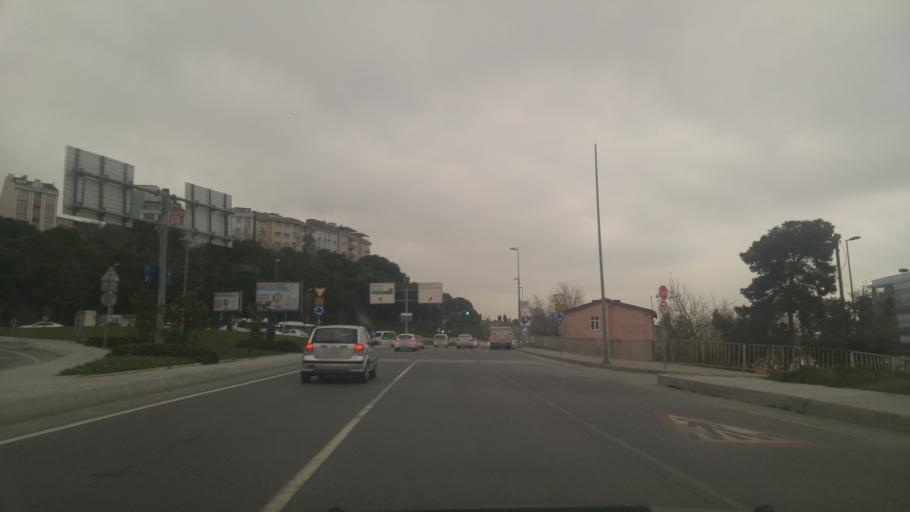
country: TR
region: Istanbul
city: Mahmutbey
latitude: 41.0203
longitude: 28.7677
